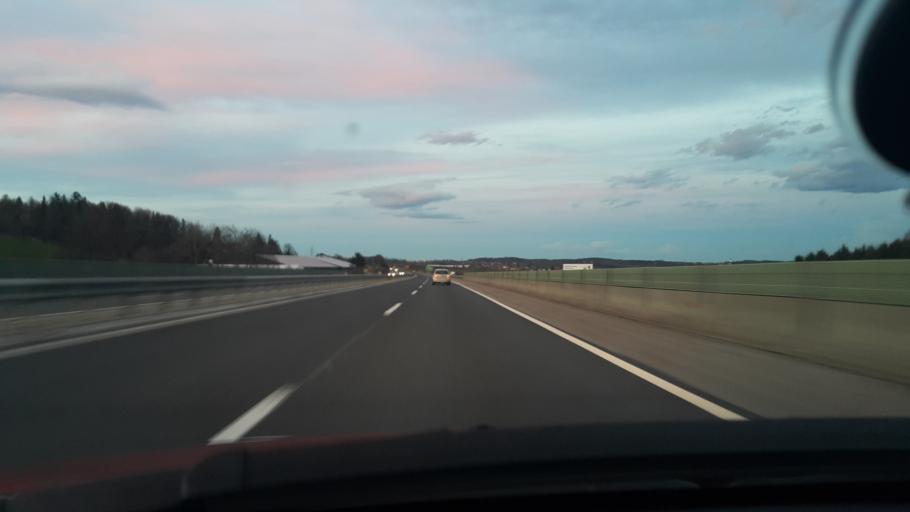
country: SI
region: Slovenska Bistrica
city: Slovenska Bistrica
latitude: 46.3749
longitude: 15.5493
